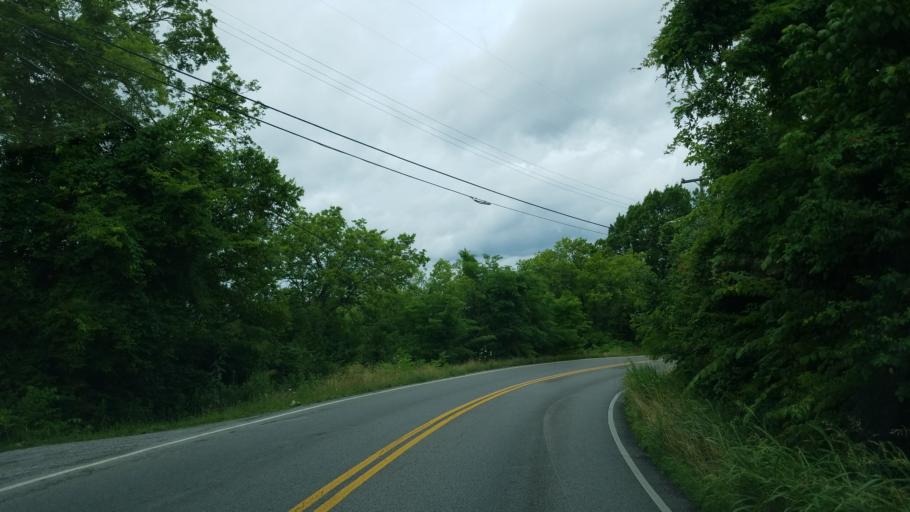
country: US
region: Tennessee
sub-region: Rutherford County
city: La Vergne
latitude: 36.0566
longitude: -86.6674
